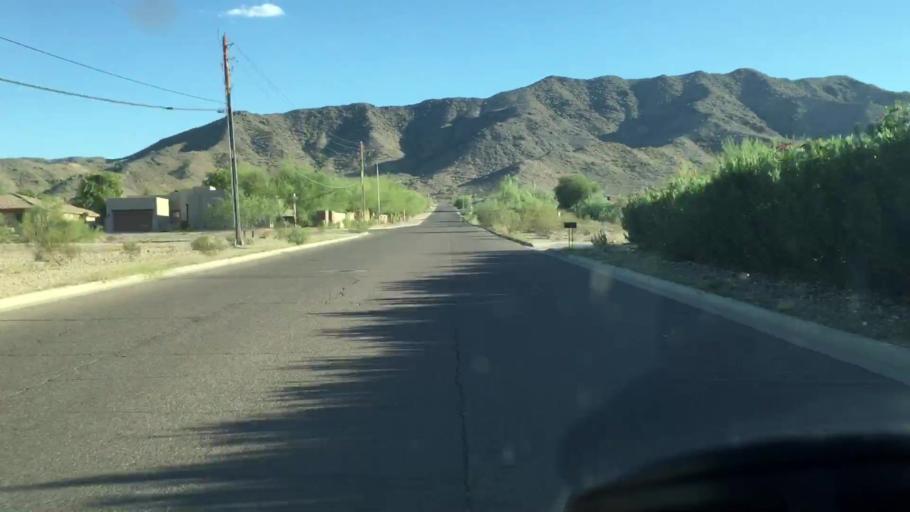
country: US
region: Arizona
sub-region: Maricopa County
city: Laveen
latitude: 33.3626
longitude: -112.0988
